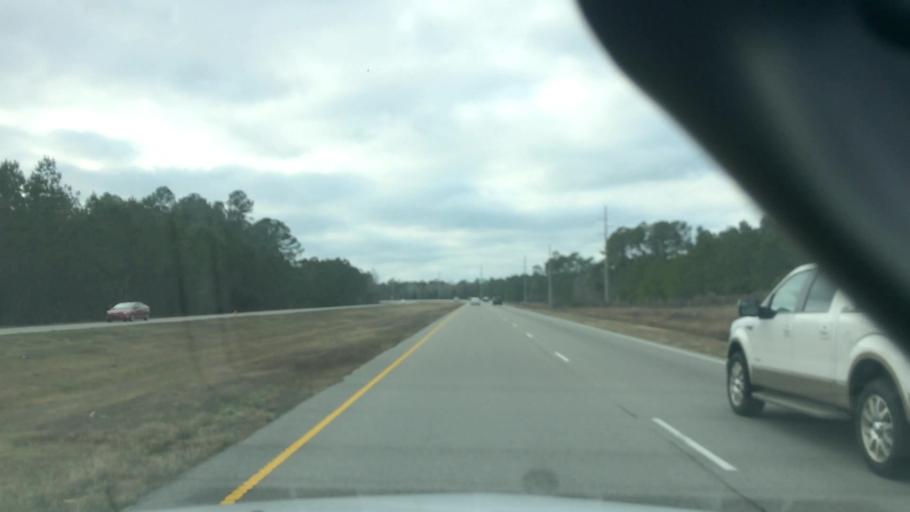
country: US
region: North Carolina
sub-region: Brunswick County
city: Shallotte
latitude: 33.9890
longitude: -78.3796
